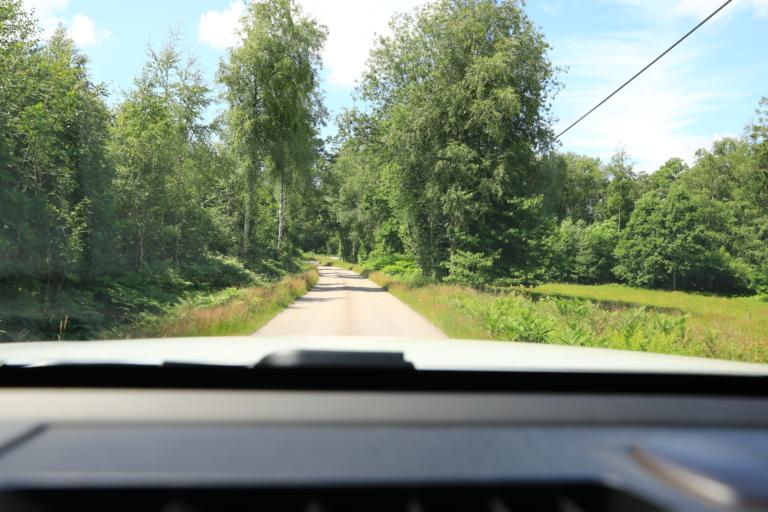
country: SE
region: Halland
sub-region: Varbergs Kommun
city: Tvaaker
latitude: 57.1036
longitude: 12.4581
